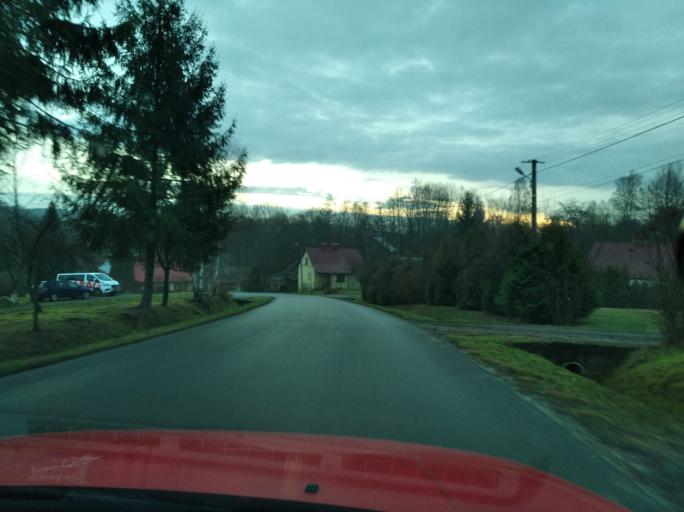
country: PL
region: Subcarpathian Voivodeship
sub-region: Powiat strzyzowski
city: Jawornik
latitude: 49.8722
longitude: 21.8739
